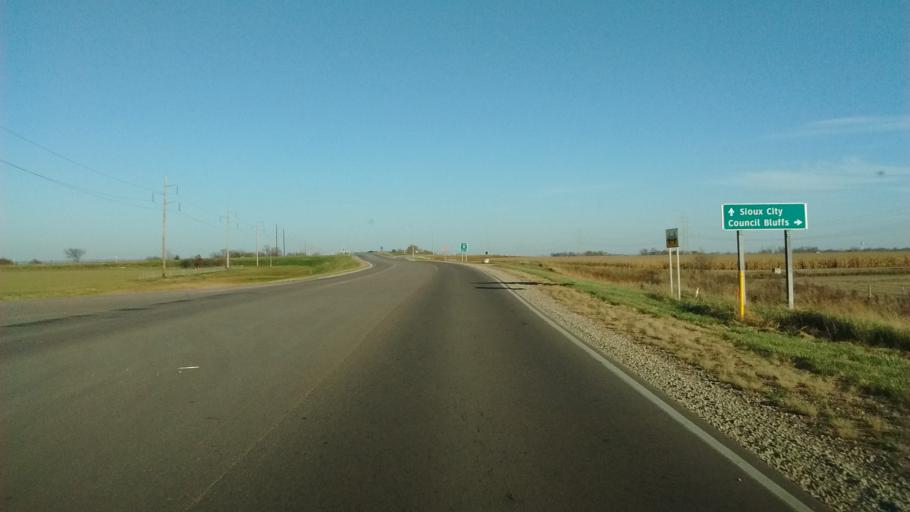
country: US
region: Iowa
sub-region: Woodbury County
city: Sergeant Bluff
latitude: 42.3301
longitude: -96.3262
